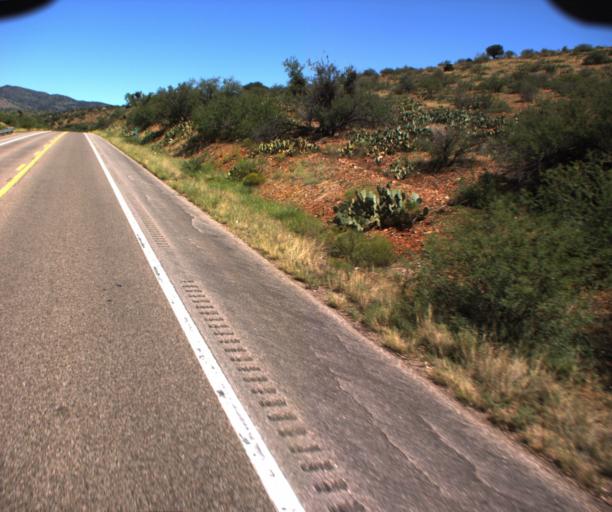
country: US
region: Arizona
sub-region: Gila County
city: Globe
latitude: 33.4641
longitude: -110.7215
